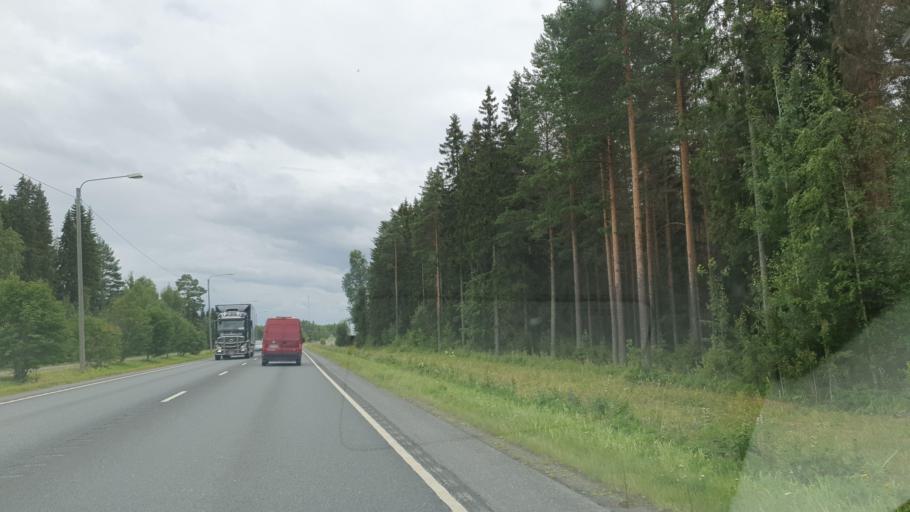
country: FI
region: Northern Savo
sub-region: Ylae-Savo
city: Lapinlahti
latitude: 63.4416
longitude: 27.3238
